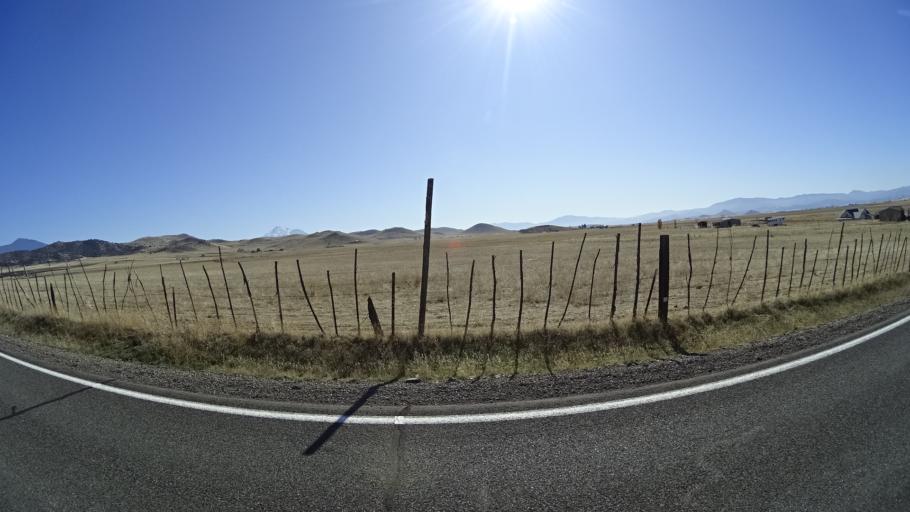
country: US
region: California
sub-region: Siskiyou County
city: Montague
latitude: 41.8082
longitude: -122.4267
